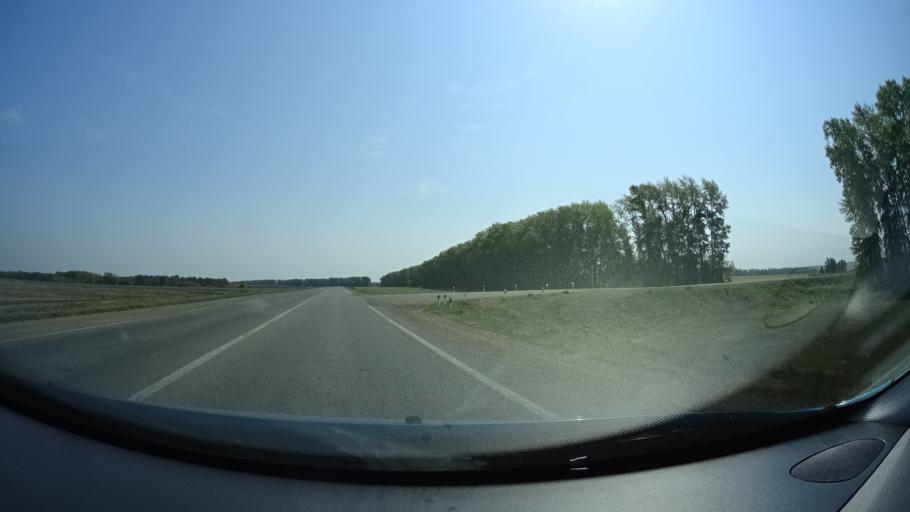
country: RU
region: Bashkortostan
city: Karmaskaly
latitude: 54.3893
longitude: 56.1272
